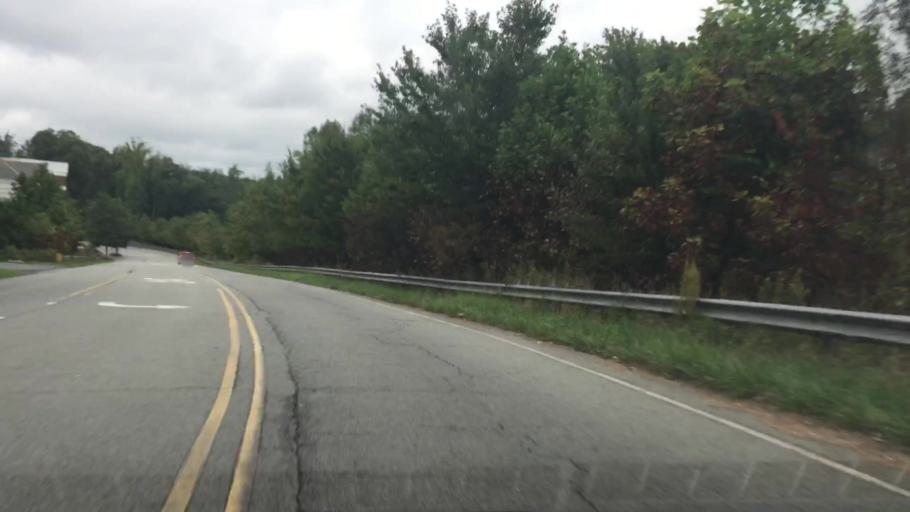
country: US
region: North Carolina
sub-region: Gaston County
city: Davidson
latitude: 35.5510
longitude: -80.8524
